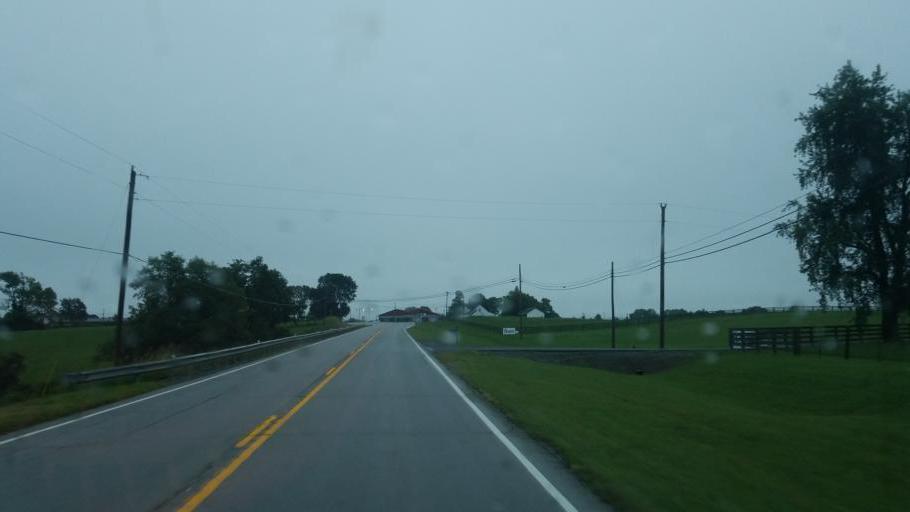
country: US
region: Kentucky
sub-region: Fleming County
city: Flemingsburg
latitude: 38.3948
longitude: -83.6941
